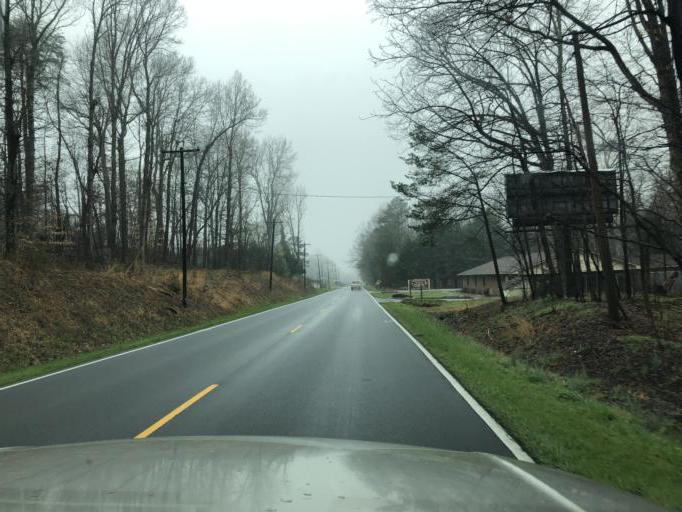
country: US
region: North Carolina
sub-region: Gaston County
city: Cherryville
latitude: 35.3730
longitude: -81.4051
